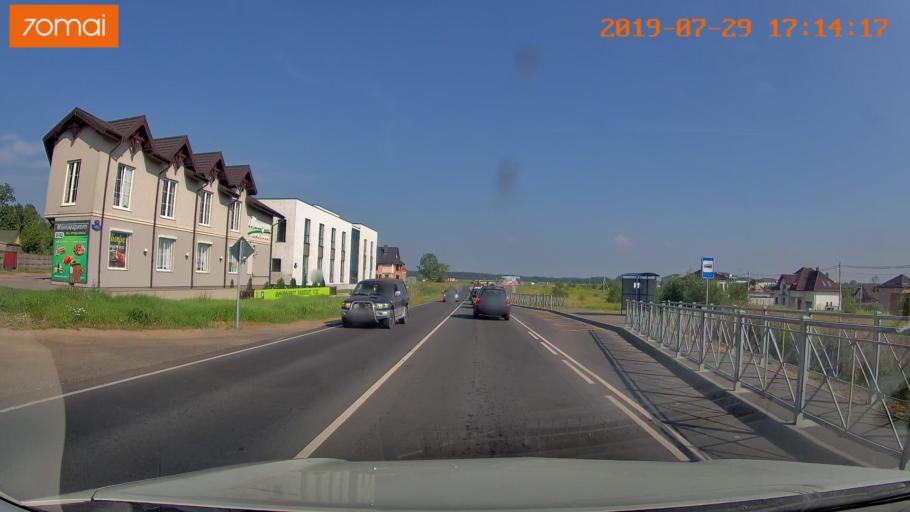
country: RU
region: Kaliningrad
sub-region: Gorod Kaliningrad
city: Kaliningrad
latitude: 54.7851
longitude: 20.4072
